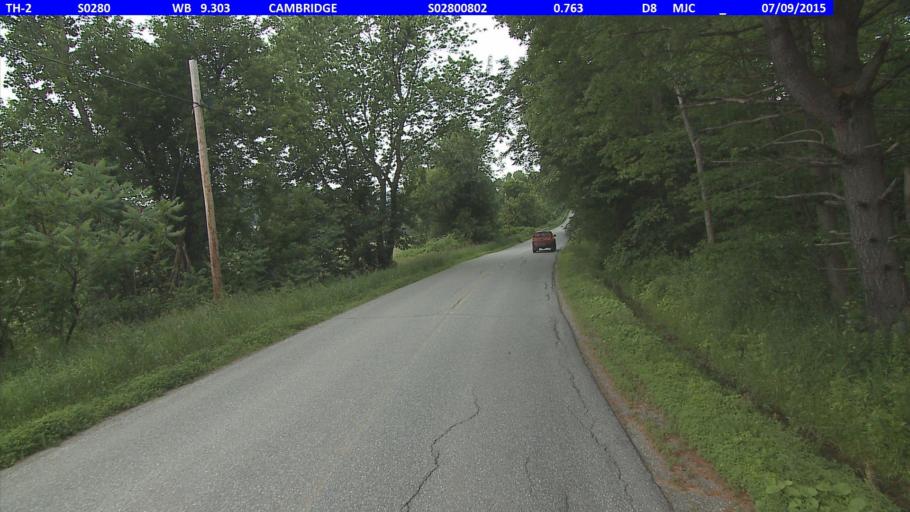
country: US
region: Vermont
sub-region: Chittenden County
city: Jericho
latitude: 44.6527
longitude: -72.8801
